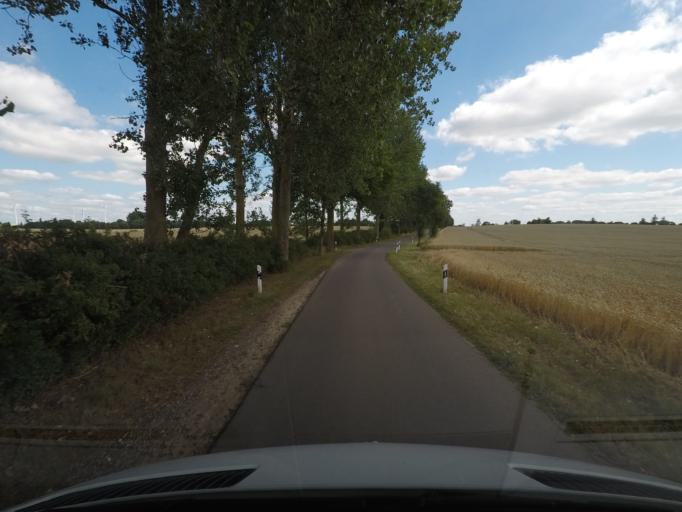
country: DE
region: Brandenburg
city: Brussow
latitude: 53.3735
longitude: 14.1433
